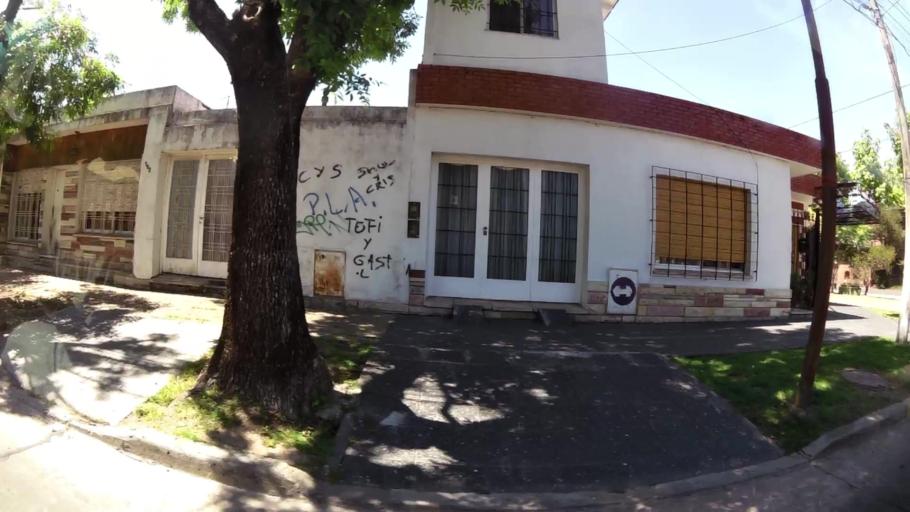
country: AR
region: Buenos Aires
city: Ituzaingo
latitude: -34.6722
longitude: -58.6879
